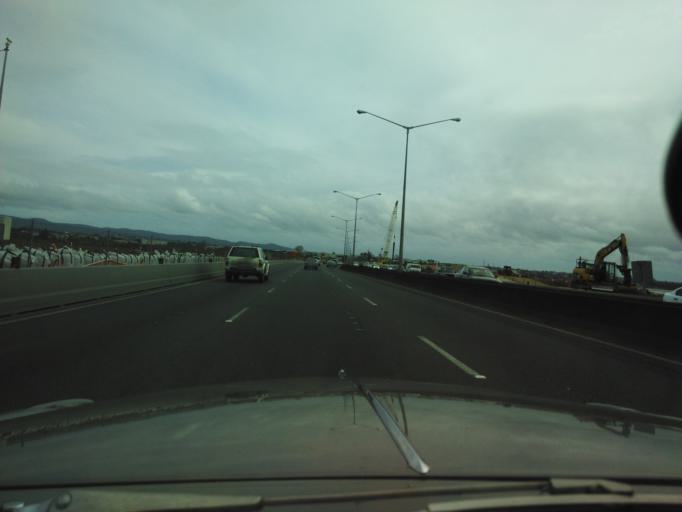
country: NZ
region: Auckland
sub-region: Auckland
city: Rosebank
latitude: -36.8721
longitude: 174.6867
